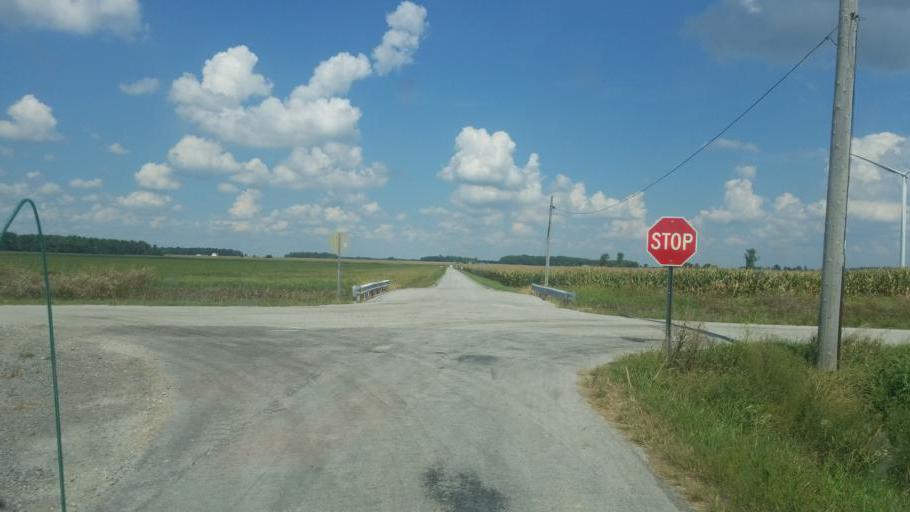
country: US
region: Ohio
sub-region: Hardin County
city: Ada
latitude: 40.7907
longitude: -83.7478
